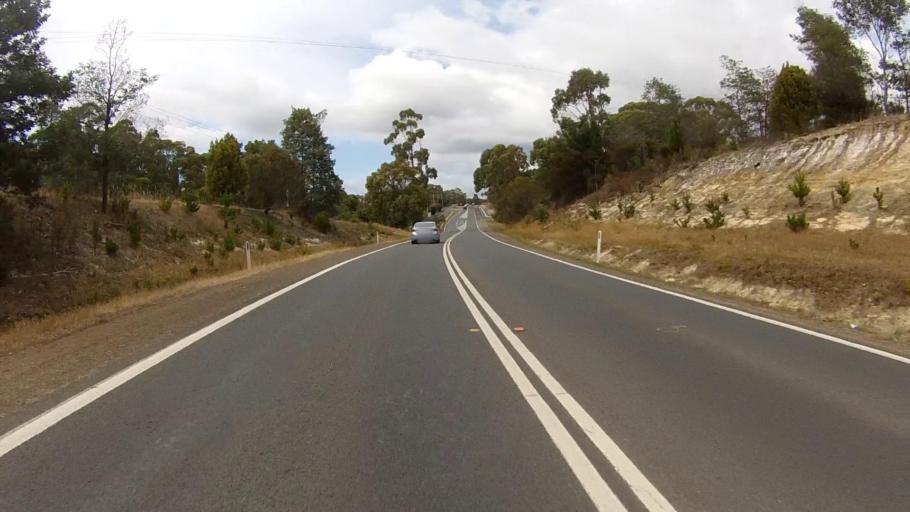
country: AU
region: Tasmania
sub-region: Kingborough
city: Margate
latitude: -43.0416
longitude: 147.2669
